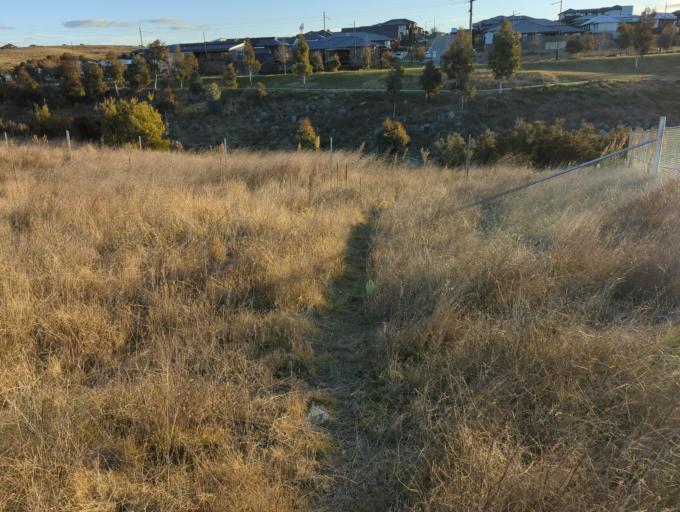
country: AU
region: New South Wales
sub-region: Queanbeyan
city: Queanbeyan
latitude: -35.4280
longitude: 149.2442
